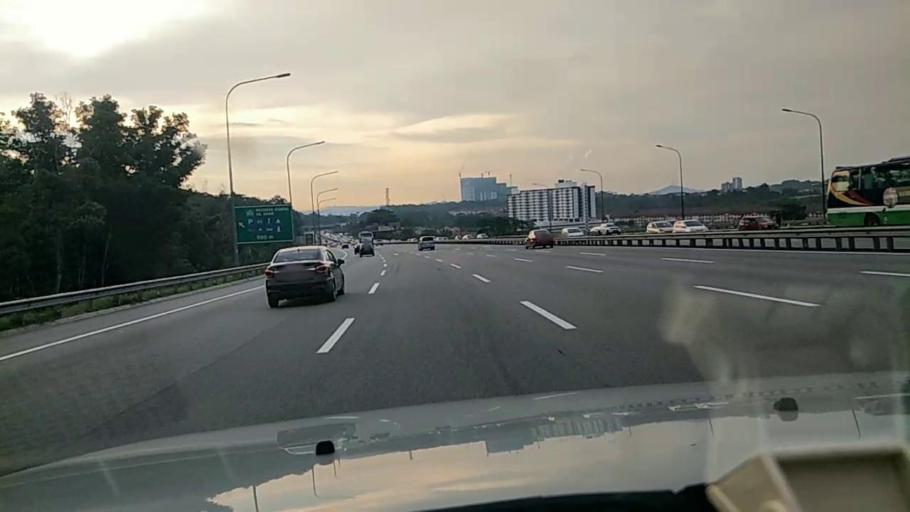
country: MY
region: Selangor
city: Kampung Baru Subang
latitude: 3.1821
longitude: 101.5974
